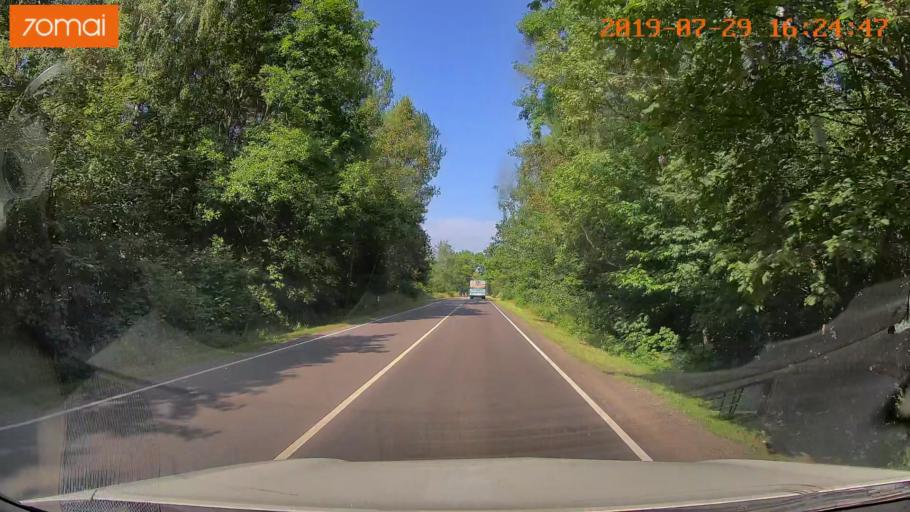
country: RU
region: Kaliningrad
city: Primorsk
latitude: 54.7174
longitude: 19.9597
